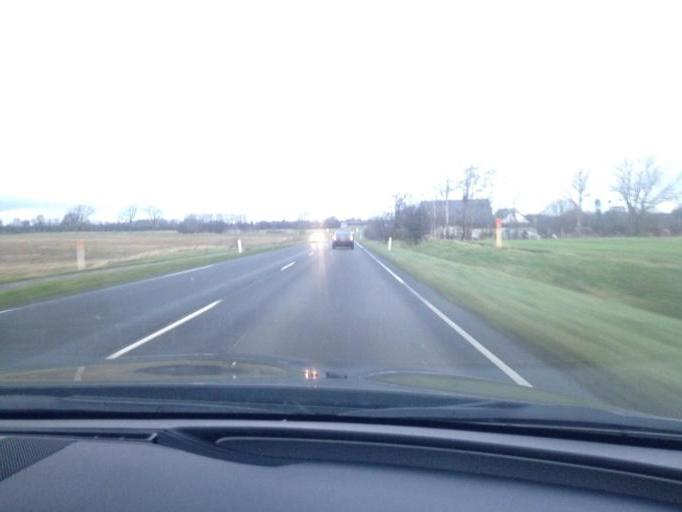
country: DK
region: South Denmark
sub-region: Kolding Kommune
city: Kolding
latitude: 55.5519
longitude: 9.4820
